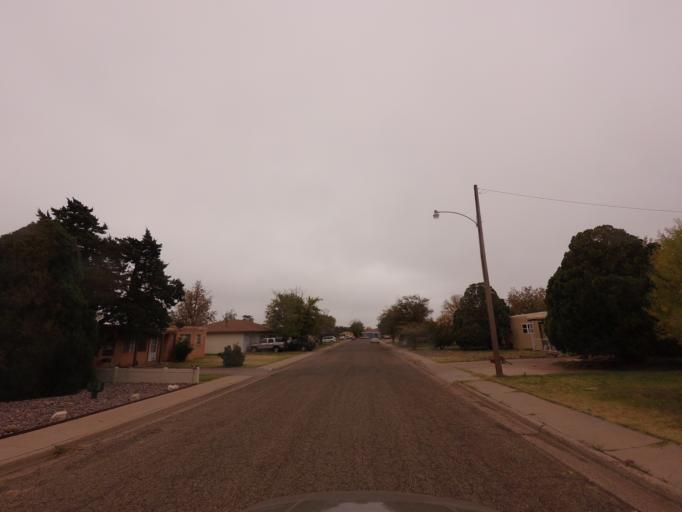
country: US
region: New Mexico
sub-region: Curry County
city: Clovis
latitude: 34.4291
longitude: -103.2086
